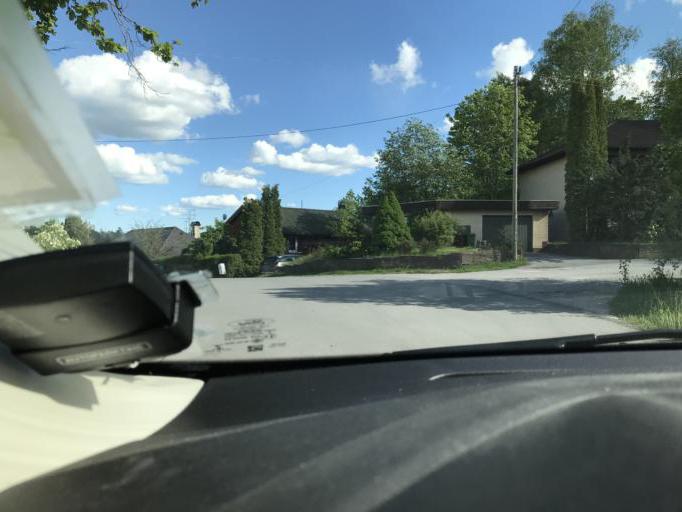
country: SE
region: Stockholm
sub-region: Botkyrka Kommun
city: Tumba
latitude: 59.1966
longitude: 17.8213
